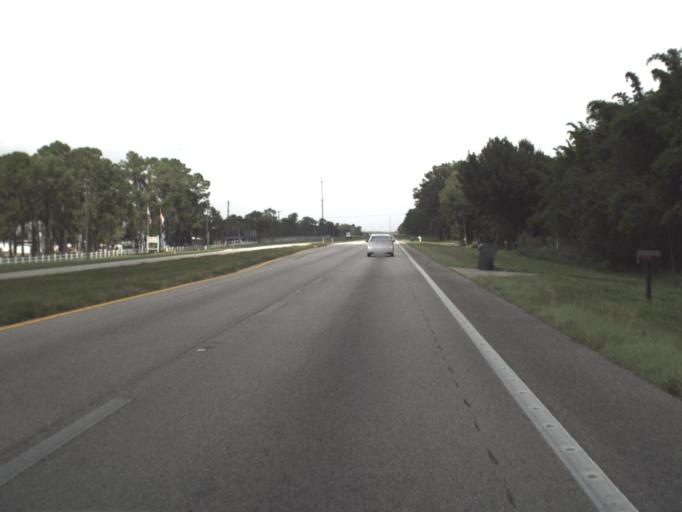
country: US
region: Florida
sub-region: Polk County
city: Crooked Lake Park
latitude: 27.7742
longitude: -81.5971
